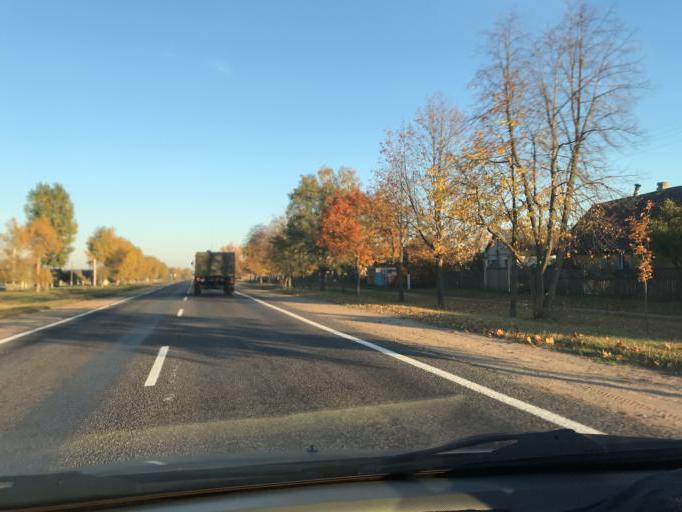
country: BY
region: Minsk
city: Staryya Darohi
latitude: 53.0458
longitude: 28.1118
